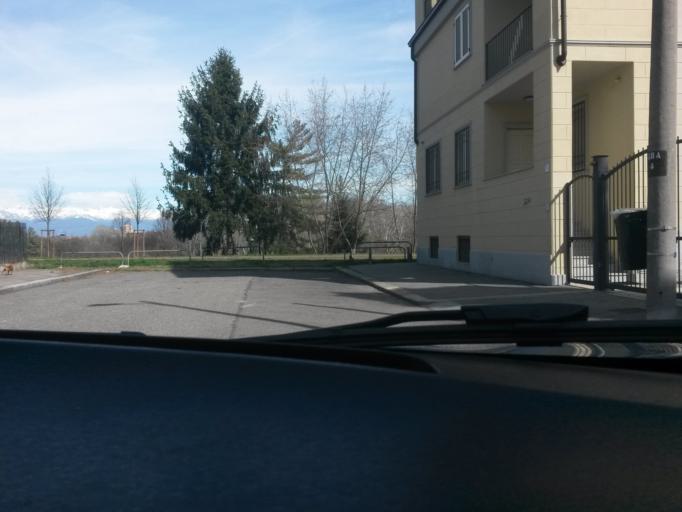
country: IT
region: Piedmont
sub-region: Provincia di Torino
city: Lesna
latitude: 45.0845
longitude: 7.6324
